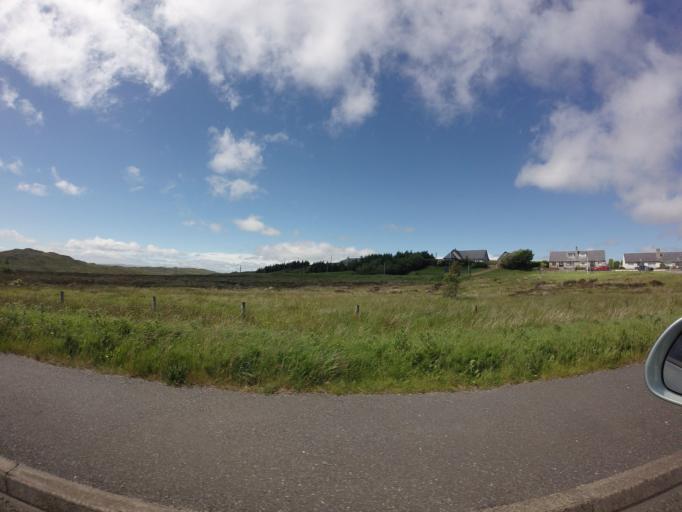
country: GB
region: Scotland
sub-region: Eilean Siar
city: Stornoway
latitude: 58.1546
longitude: -6.4990
